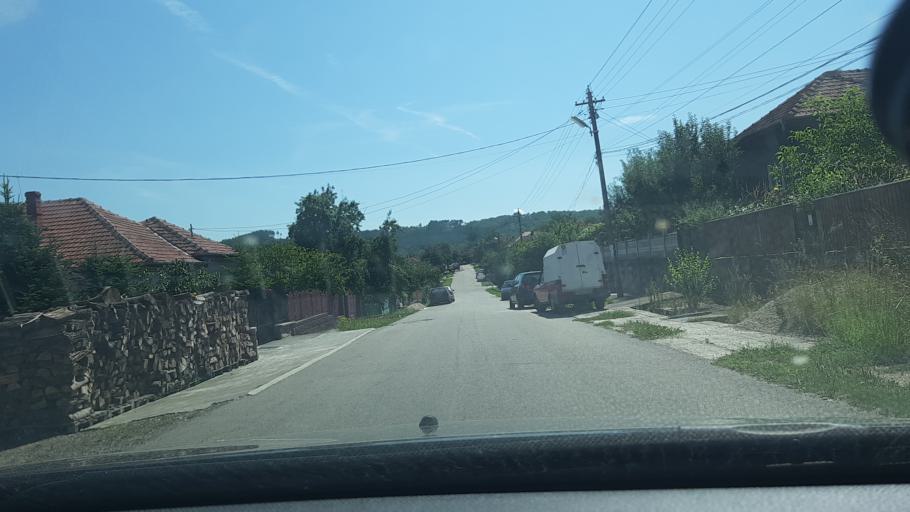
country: RO
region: Hunedoara
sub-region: Comuna Teliucu Inferior
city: Teliucu Inferior
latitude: 45.7001
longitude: 22.8903
